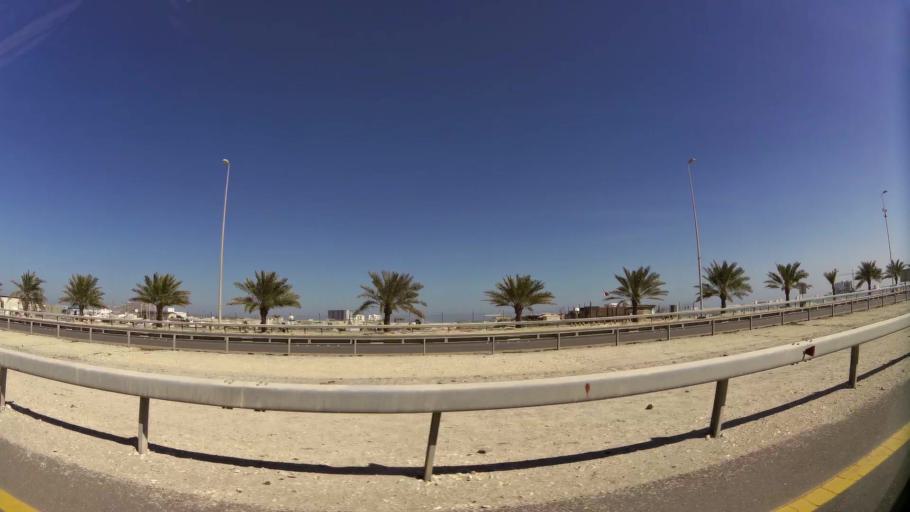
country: BH
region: Muharraq
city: Al Hadd
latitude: 26.2679
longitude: 50.6618
